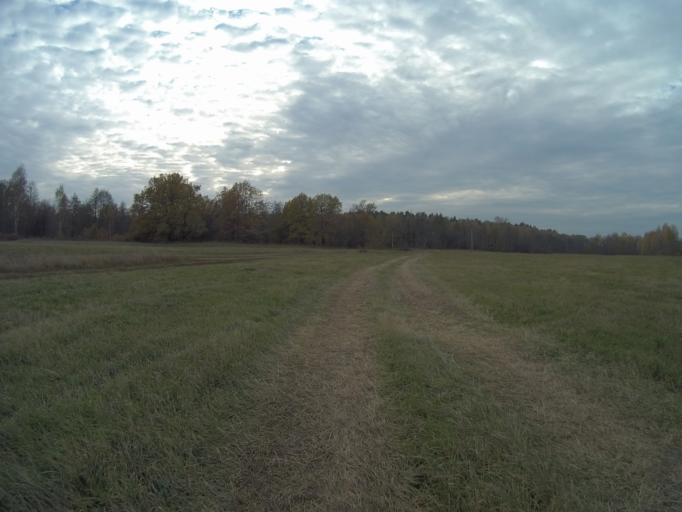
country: RU
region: Vladimir
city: Orgtrud
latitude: 56.1687
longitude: 40.5979
